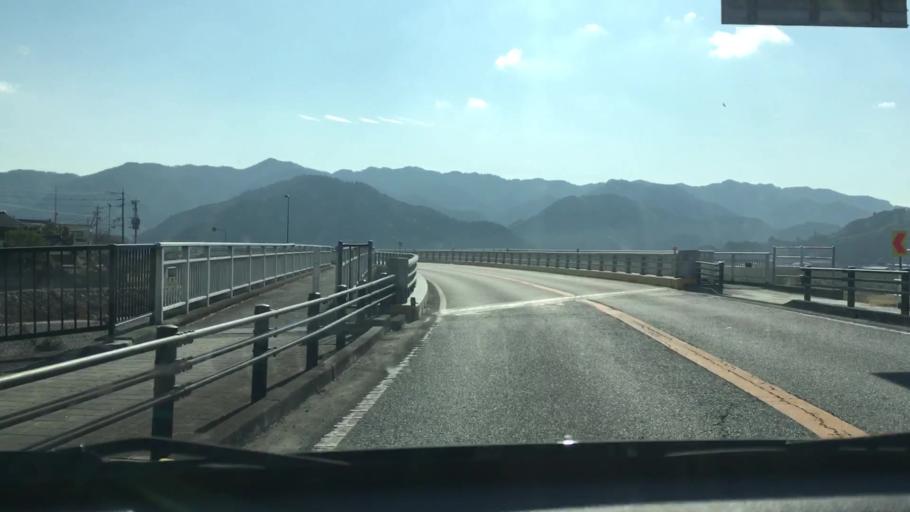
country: JP
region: Oita
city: Saiki
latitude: 32.9628
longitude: 131.8380
